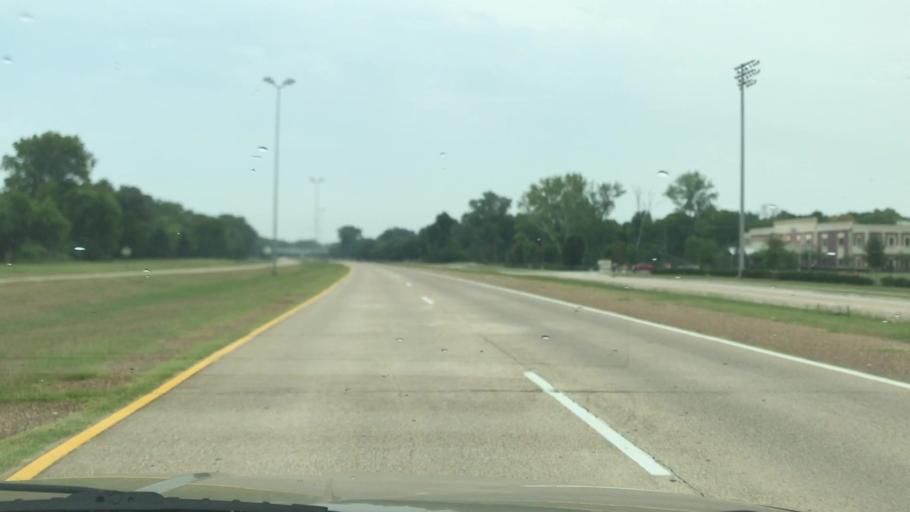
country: US
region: Louisiana
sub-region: Bossier Parish
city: Bossier City
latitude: 32.4971
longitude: -93.7115
